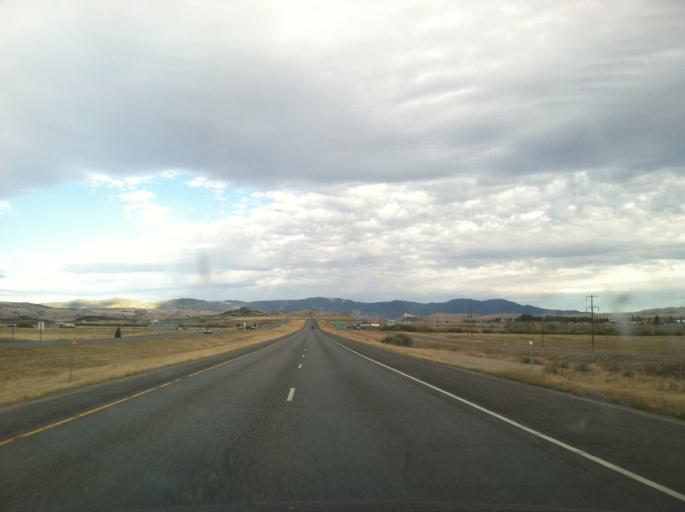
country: US
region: Montana
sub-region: Silver Bow County
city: Butte-Silver Bow (Balance)
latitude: 46.0100
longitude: -112.7022
